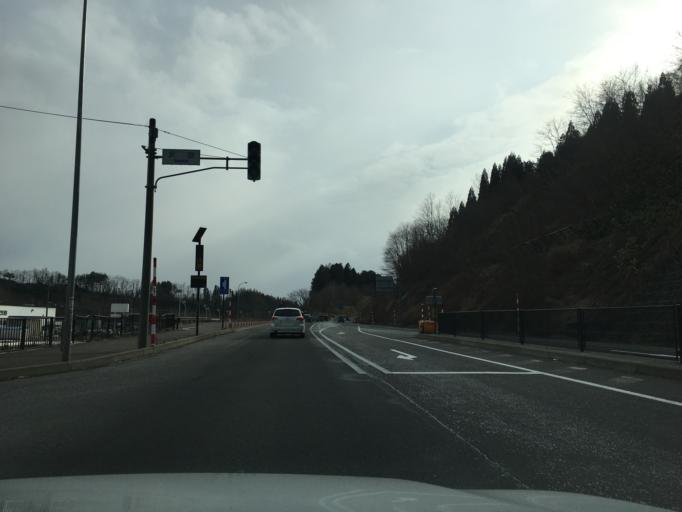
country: JP
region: Aomori
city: Namioka
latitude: 40.7736
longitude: 140.5992
